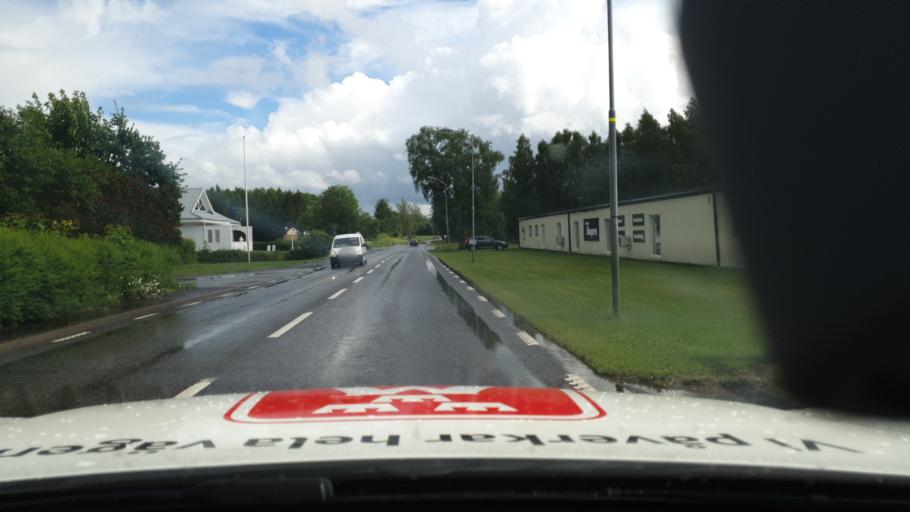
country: SE
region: Vaestra Goetaland
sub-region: Falkopings Kommun
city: Falkoeping
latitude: 58.0714
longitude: 13.5230
